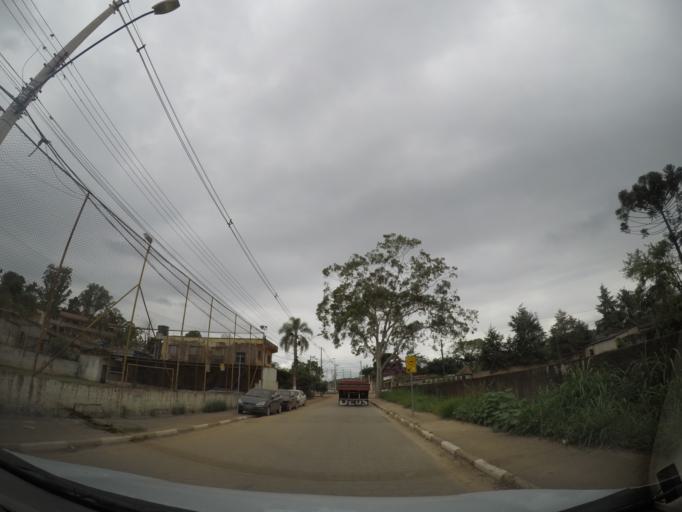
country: BR
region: Sao Paulo
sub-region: Aruja
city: Aruja
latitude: -23.3677
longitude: -46.4020
